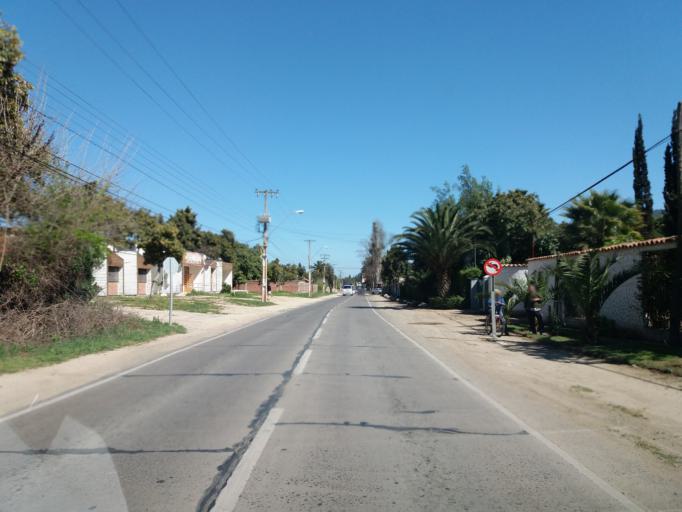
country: CL
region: Valparaiso
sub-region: Provincia de Marga Marga
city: Limache
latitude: -32.9970
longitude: -71.2223
